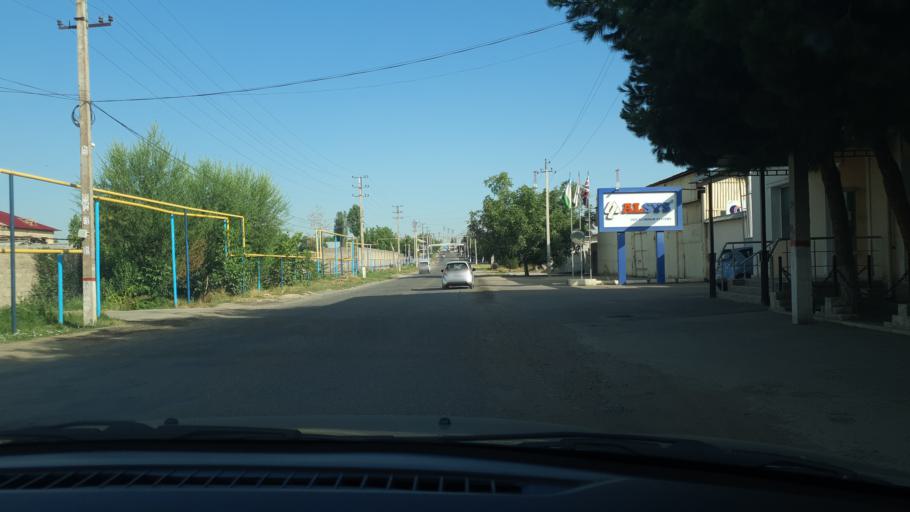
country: UZ
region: Toshkent
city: Urtaowul
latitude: 41.2043
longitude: 69.1516
